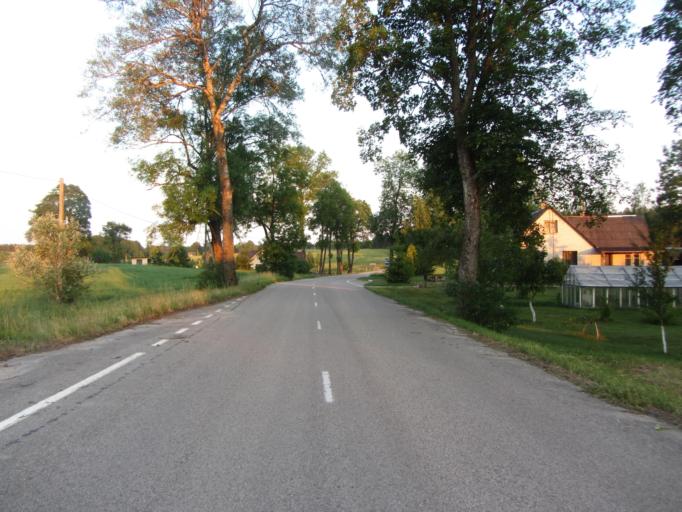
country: LT
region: Alytaus apskritis
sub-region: Alytaus rajonas
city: Daugai
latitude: 54.3936
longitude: 24.3478
